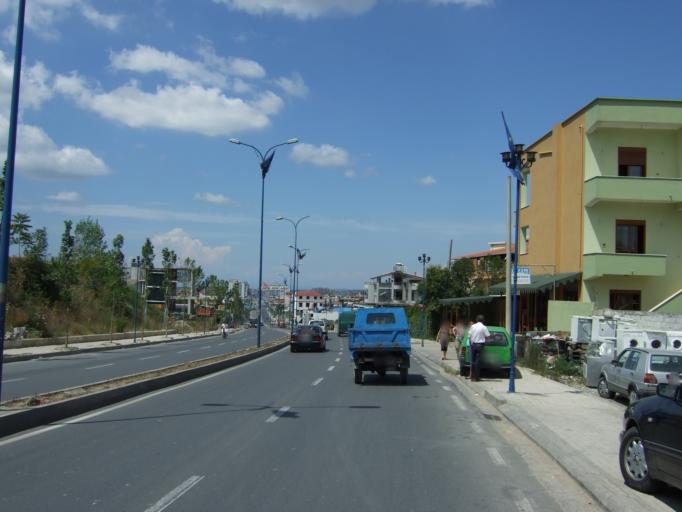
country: AL
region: Tirane
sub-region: Rrethi i Tiranes
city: Kamez
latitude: 41.3632
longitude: 19.7718
